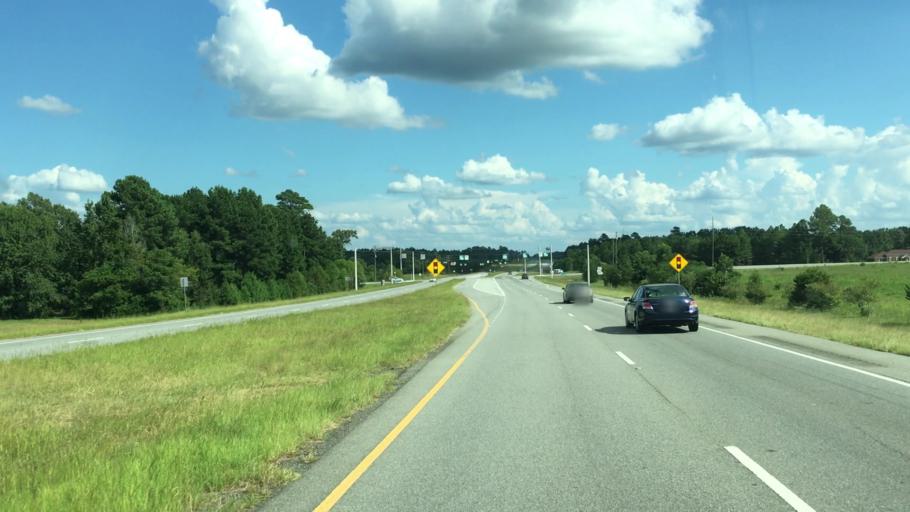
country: US
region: Georgia
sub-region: Laurens County
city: Dublin
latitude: 32.5178
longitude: -82.9587
